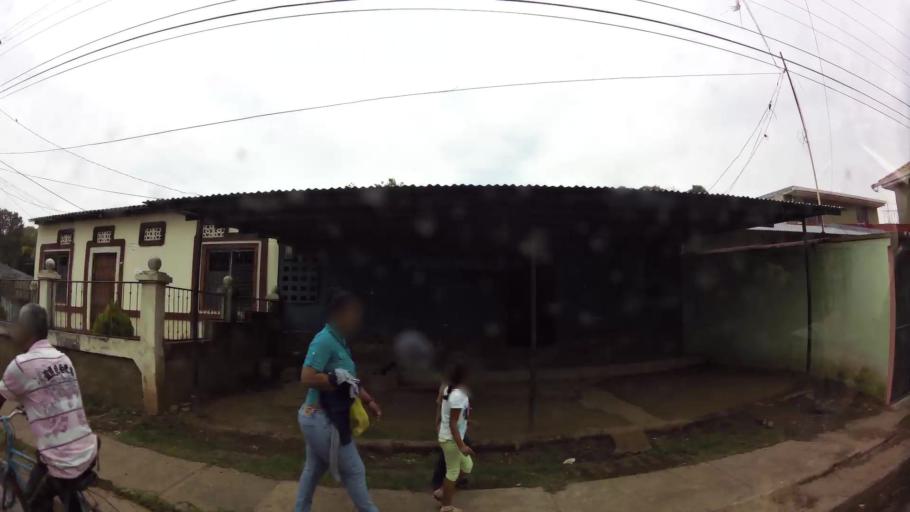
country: NI
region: Granada
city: Nandaime
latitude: 11.7591
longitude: -86.0578
